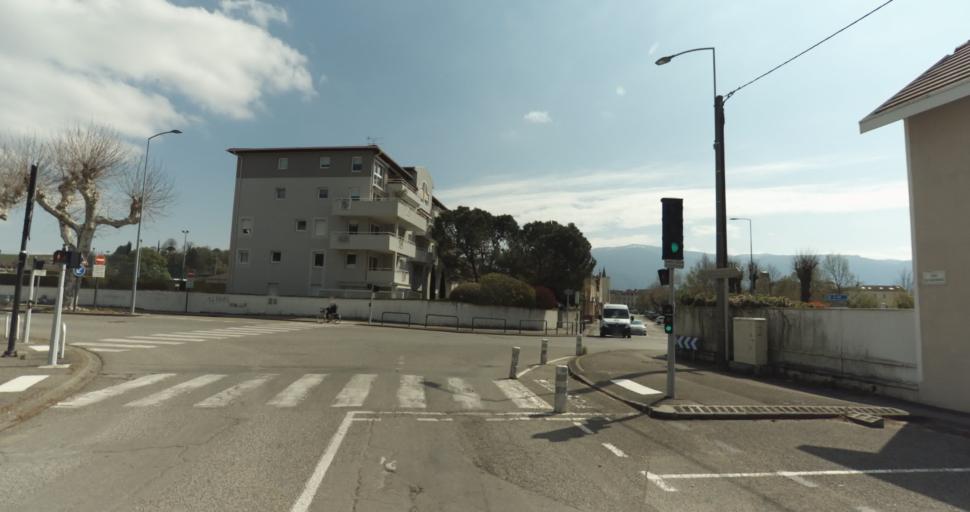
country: FR
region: Rhone-Alpes
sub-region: Departement de l'Isere
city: Saint-Marcellin
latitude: 45.1557
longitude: 5.3171
